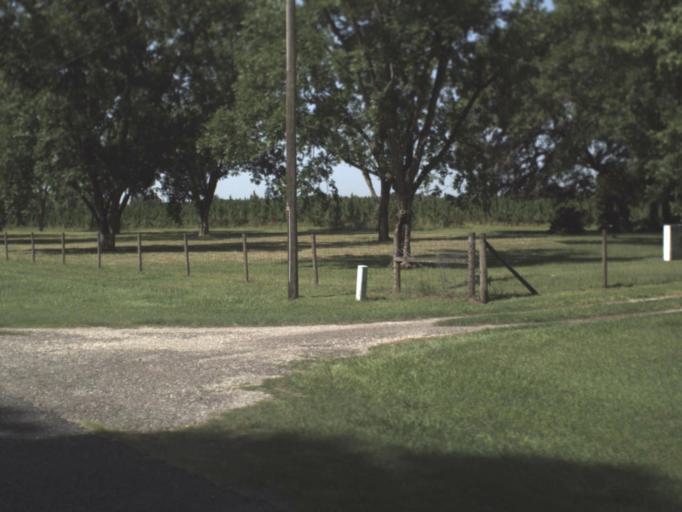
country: US
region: Florida
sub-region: Gilchrist County
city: Trenton
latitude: 29.5606
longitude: -82.8231
